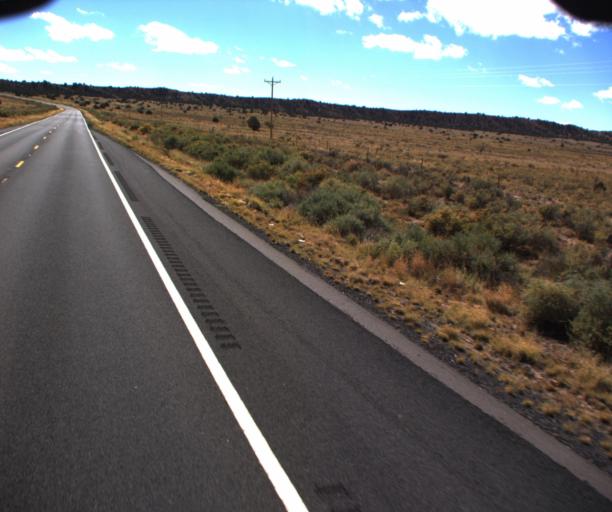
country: US
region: Arizona
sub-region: Apache County
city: Houck
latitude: 35.0425
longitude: -109.2698
